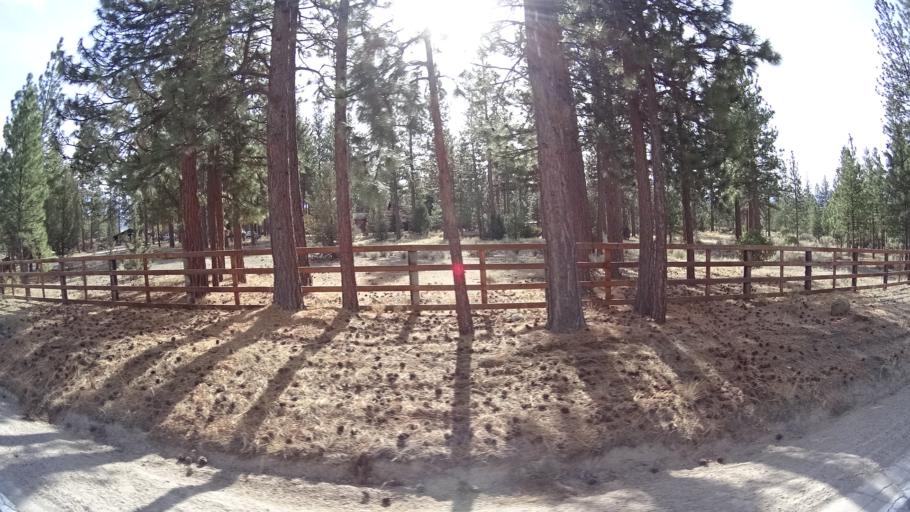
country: US
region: California
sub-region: Siskiyou County
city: Weed
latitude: 41.4940
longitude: -122.3755
